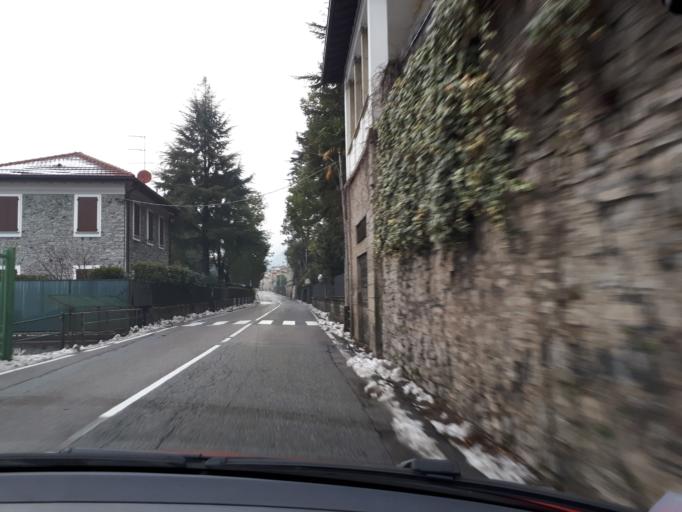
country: IT
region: Lombardy
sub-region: Provincia di Lecco
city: Lierna
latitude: 45.9569
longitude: 9.3020
